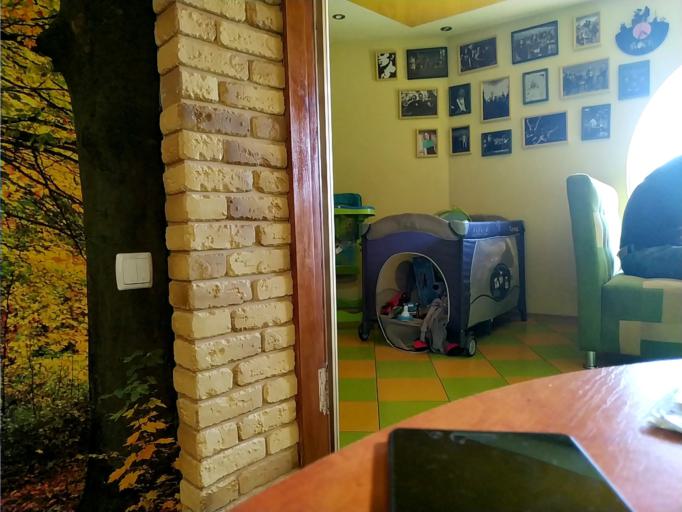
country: RU
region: Rjazan
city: Putyatino
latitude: 53.9962
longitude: 41.2583
